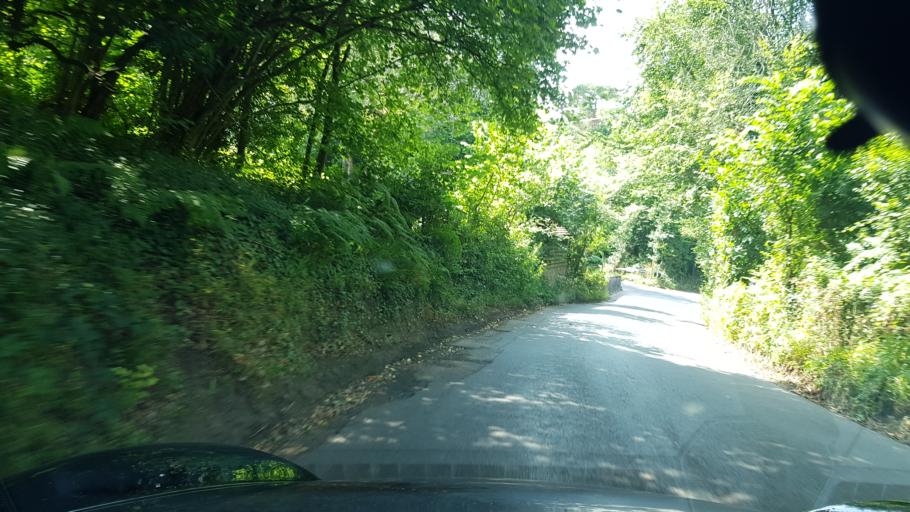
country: GB
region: England
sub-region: Surrey
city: Elstead
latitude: 51.1502
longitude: -0.7180
